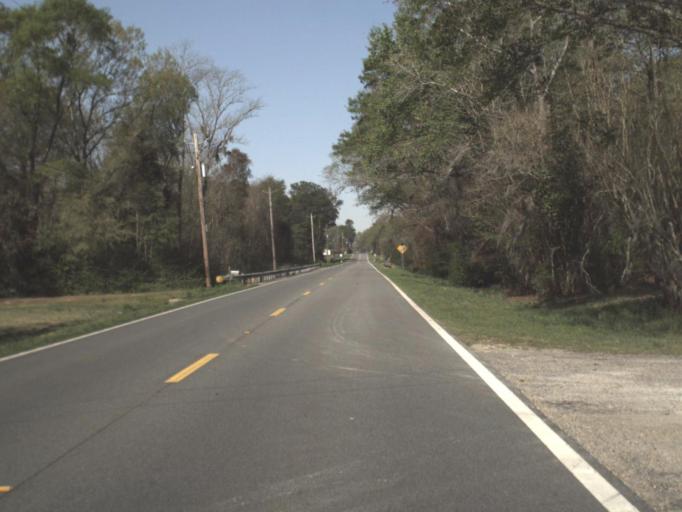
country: US
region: Florida
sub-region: Jackson County
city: Graceville
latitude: 30.9562
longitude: -85.4907
